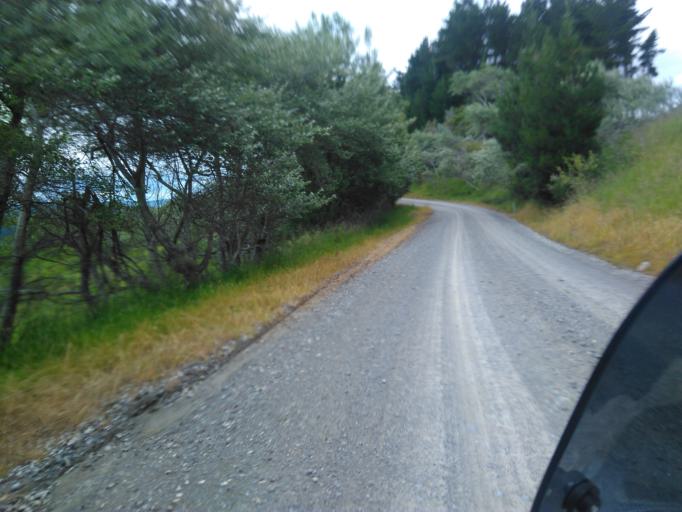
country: NZ
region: Gisborne
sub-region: Gisborne District
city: Gisborne
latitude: -38.0500
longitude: 178.0895
